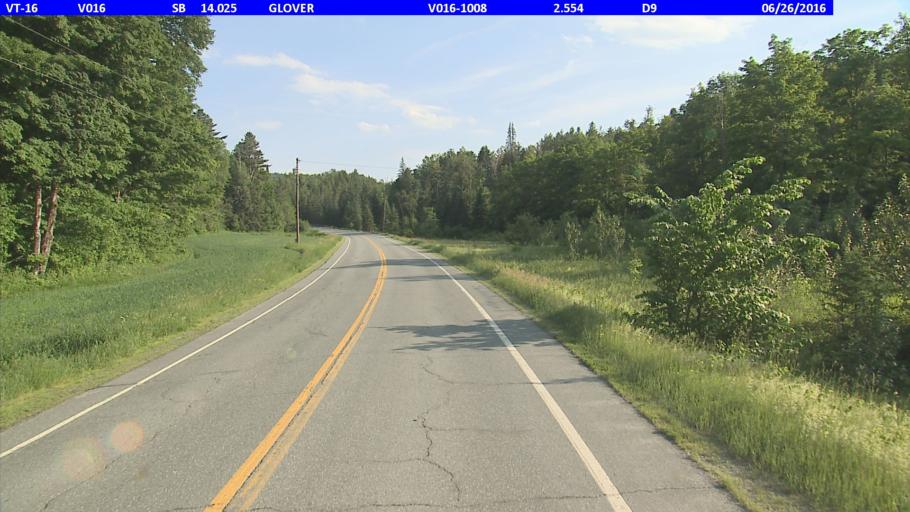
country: US
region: Vermont
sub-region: Caledonia County
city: Hardwick
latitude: 44.6607
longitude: -72.1983
